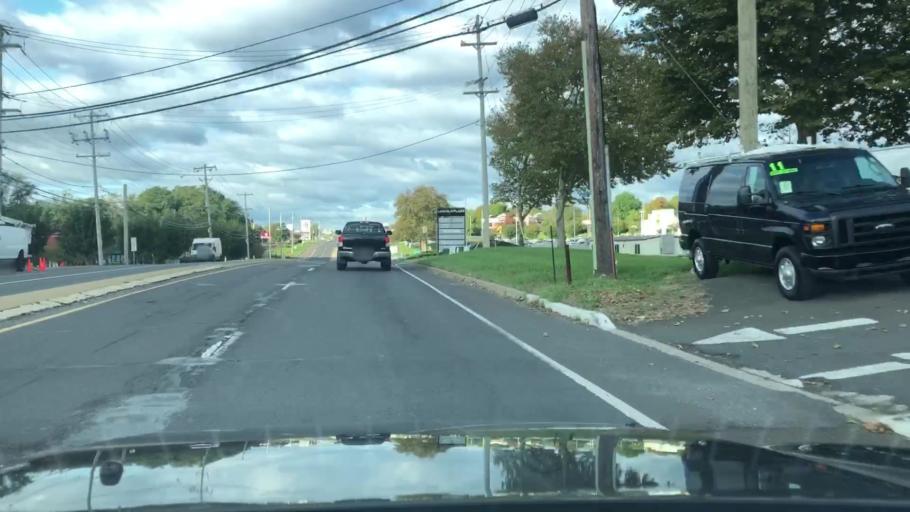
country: US
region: Pennsylvania
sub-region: Bucks County
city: Fairless Hills
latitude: 40.1805
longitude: -74.8711
